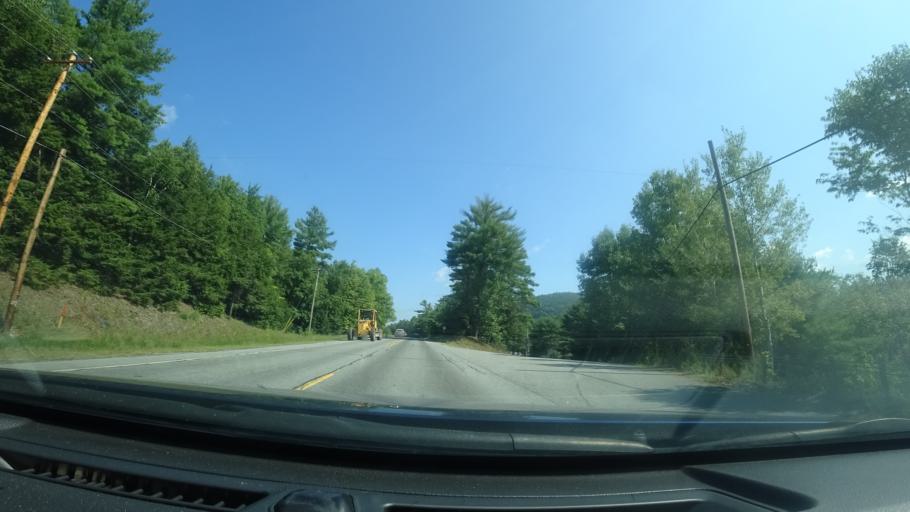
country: US
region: New York
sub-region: Warren County
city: Warrensburg
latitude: 43.6344
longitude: -73.7982
